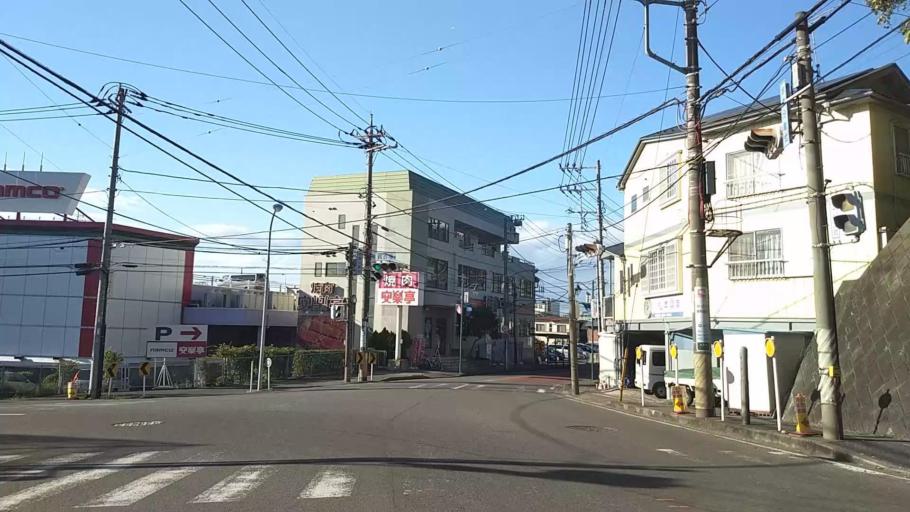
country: JP
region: Tokyo
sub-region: Machida-shi
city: Machida
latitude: 35.5197
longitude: 139.5543
